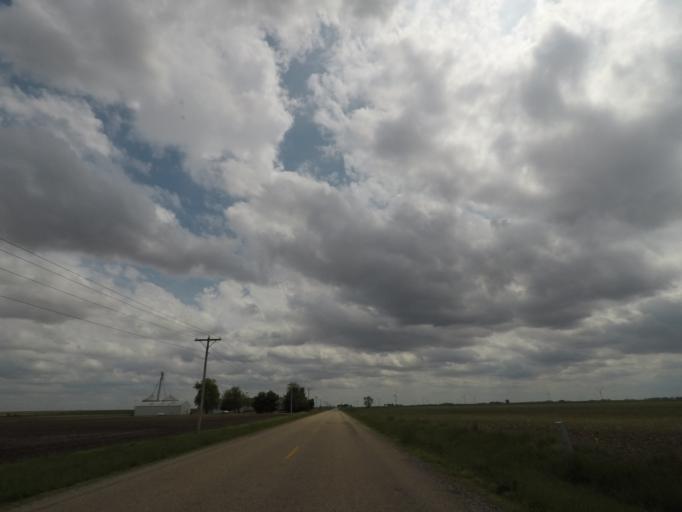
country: US
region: Illinois
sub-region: Macon County
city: Maroa
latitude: 40.0766
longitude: -89.0860
